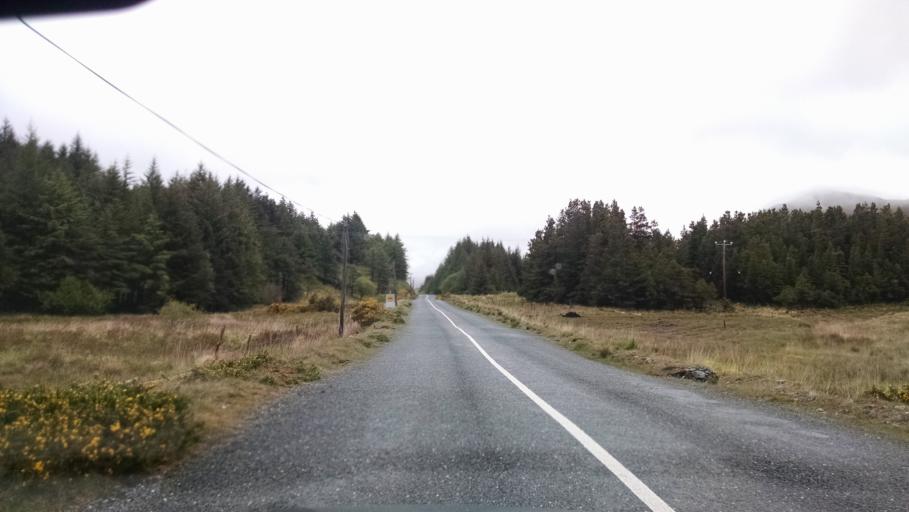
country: IE
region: Connaught
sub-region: County Galway
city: Clifden
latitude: 53.4701
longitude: -9.7483
